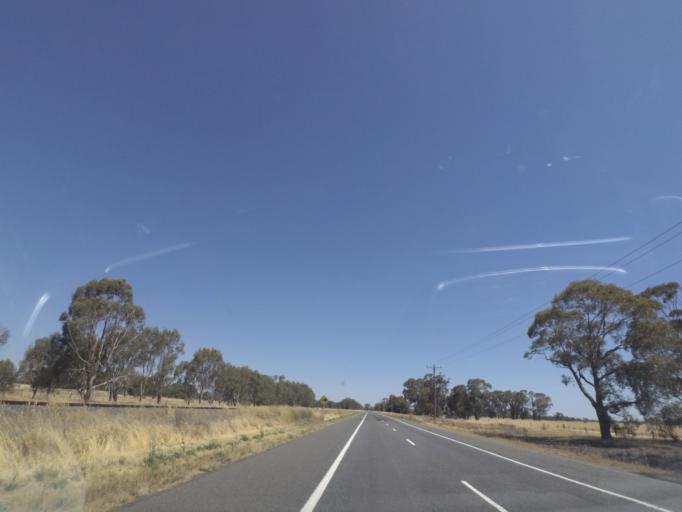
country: AU
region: Victoria
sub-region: Greater Shepparton
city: Shepparton
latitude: -36.2174
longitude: 145.4318
